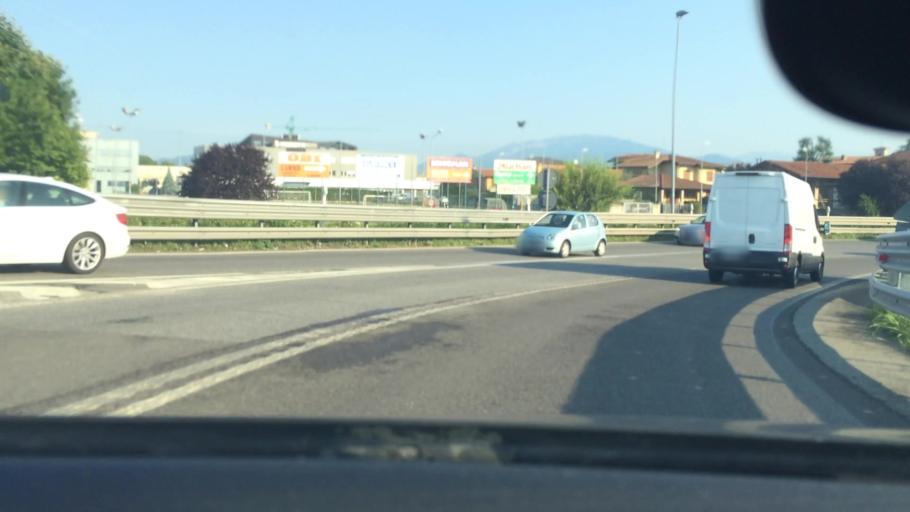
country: IT
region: Lombardy
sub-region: Provincia di Bergamo
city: Dalmine
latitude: 45.6450
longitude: 9.6195
